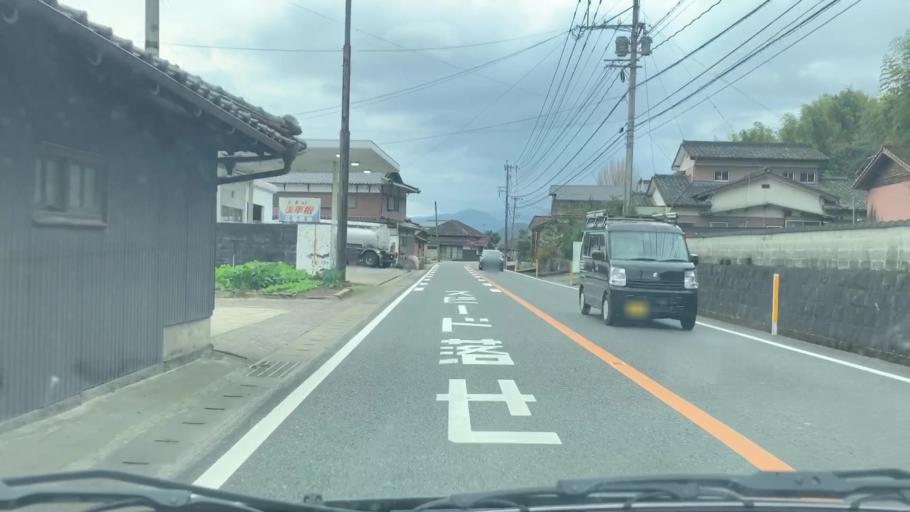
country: JP
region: Saga Prefecture
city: Kashima
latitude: 33.1394
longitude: 130.0638
